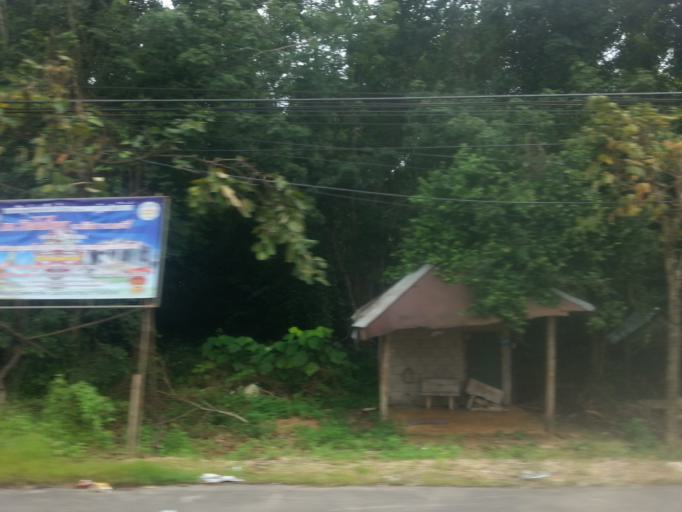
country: TH
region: Krabi
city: Krabi
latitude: 8.0832
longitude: 98.8949
